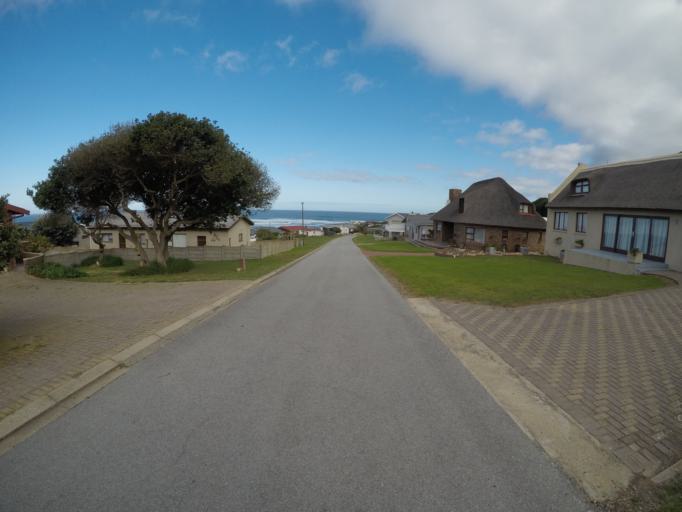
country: ZA
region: Western Cape
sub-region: Eden District Municipality
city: Riversdale
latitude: -34.4262
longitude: 21.3352
